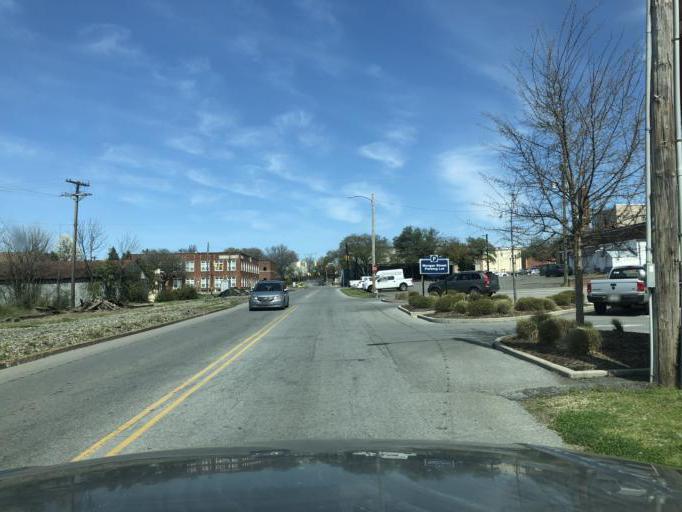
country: US
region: North Carolina
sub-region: Cleveland County
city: Shelby
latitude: 35.2899
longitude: -81.5420
